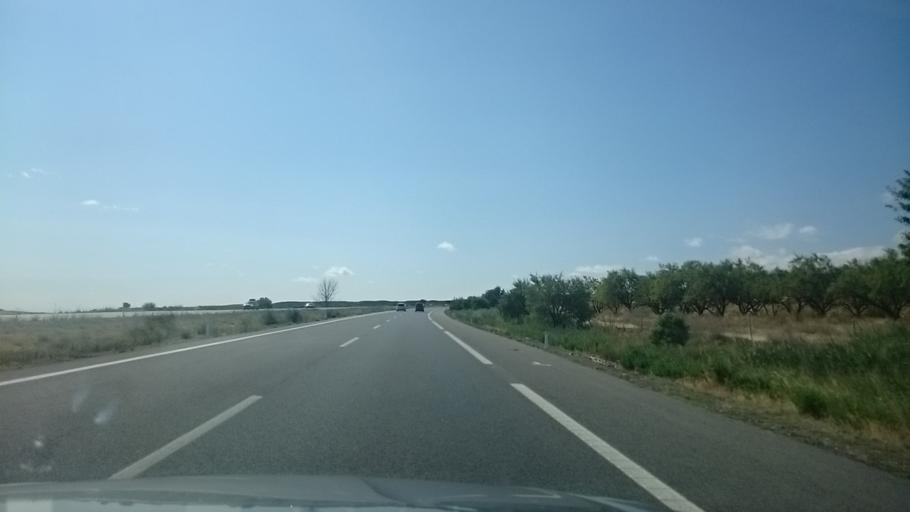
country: ES
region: Navarre
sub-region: Provincia de Navarra
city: Ribaforada
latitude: 41.9546
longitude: -1.5362
